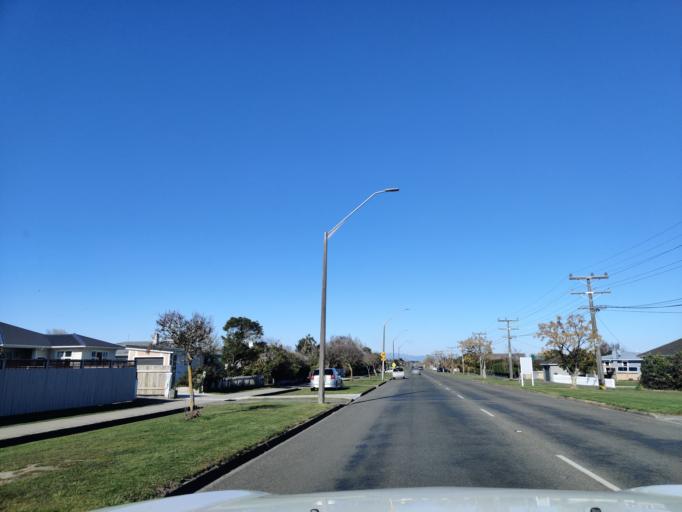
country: NZ
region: Manawatu-Wanganui
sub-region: Palmerston North City
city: Palmerston North
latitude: -40.2207
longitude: 175.5786
